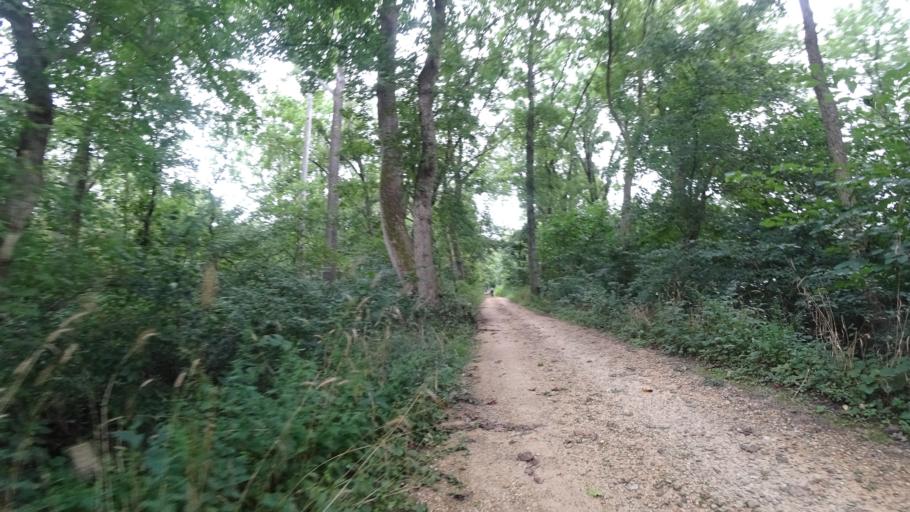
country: US
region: Virginia
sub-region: Loudoun County
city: Lowes Island
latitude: 39.0677
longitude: -77.3634
